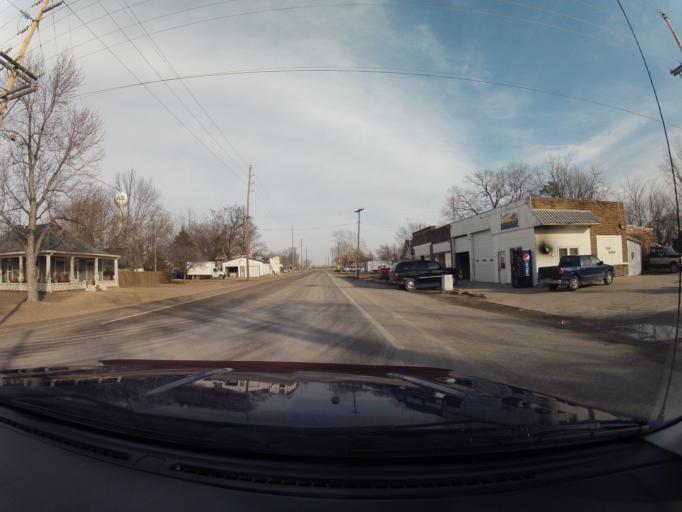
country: US
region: Kansas
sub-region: Pottawatomie County
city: Saint Marys
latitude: 39.2158
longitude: -96.1793
